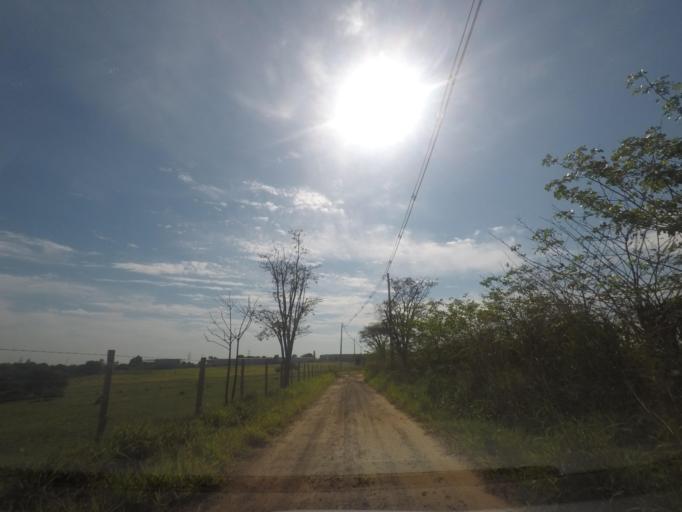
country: BR
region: Sao Paulo
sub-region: Sumare
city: Sumare
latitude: -22.7852
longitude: -47.2388
